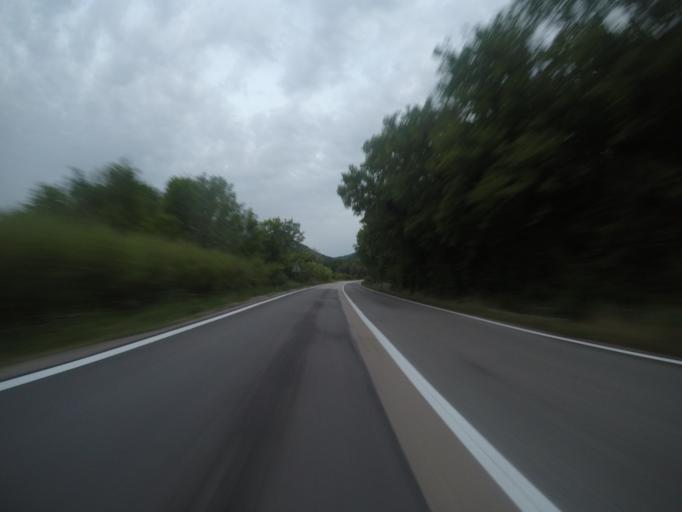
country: ME
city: Petrovac na Moru
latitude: 42.1973
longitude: 18.9705
